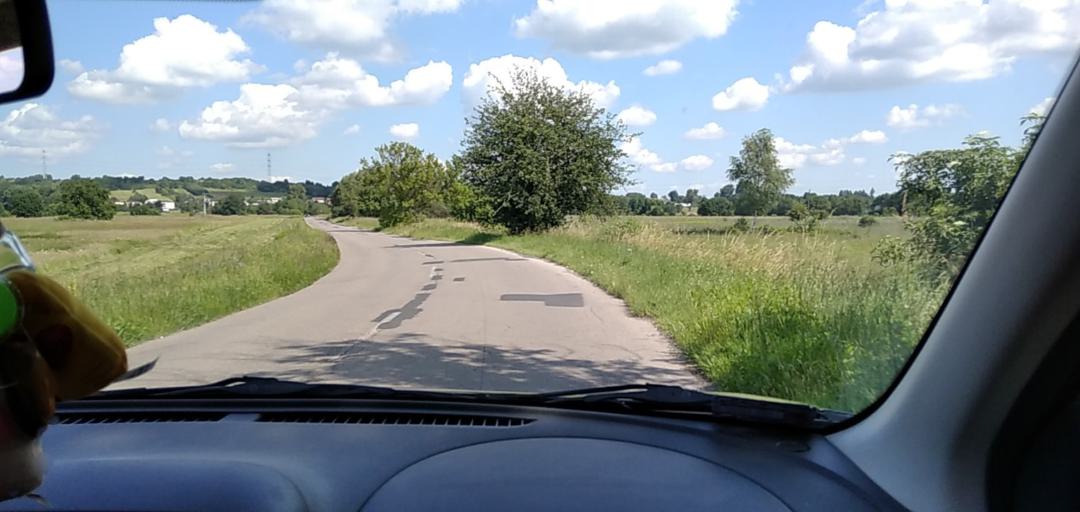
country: PL
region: Silesian Voivodeship
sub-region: Powiat bedzinski
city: Sarnow
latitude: 50.3949
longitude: 19.1394
